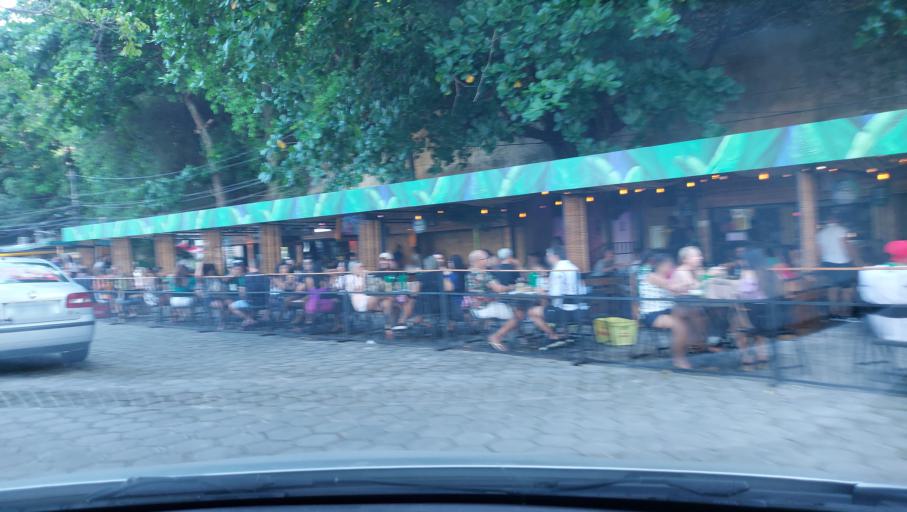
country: BR
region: Bahia
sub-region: Salvador
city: Salvador
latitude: -12.9789
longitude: -38.4451
